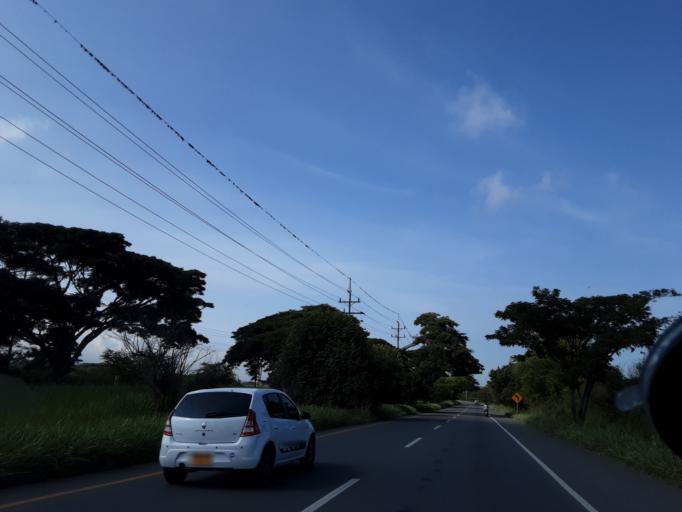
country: CO
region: Valle del Cauca
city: Buga
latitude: 3.8839
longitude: -76.3131
